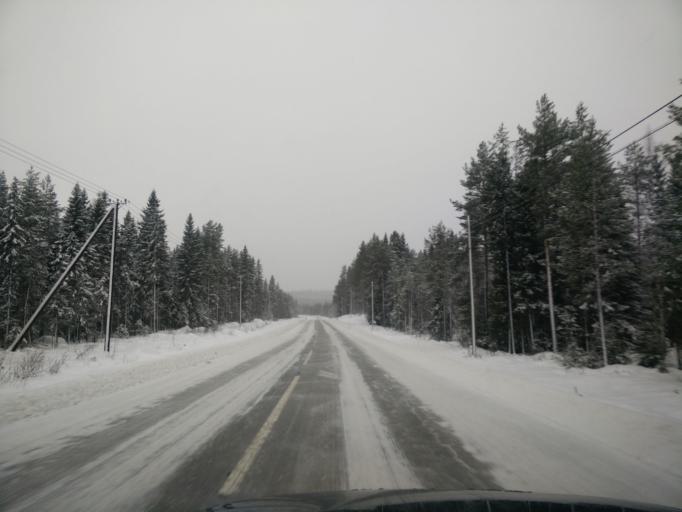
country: SE
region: Jaemtland
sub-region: Braecke Kommun
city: Braecke
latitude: 62.3975
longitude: 15.1651
